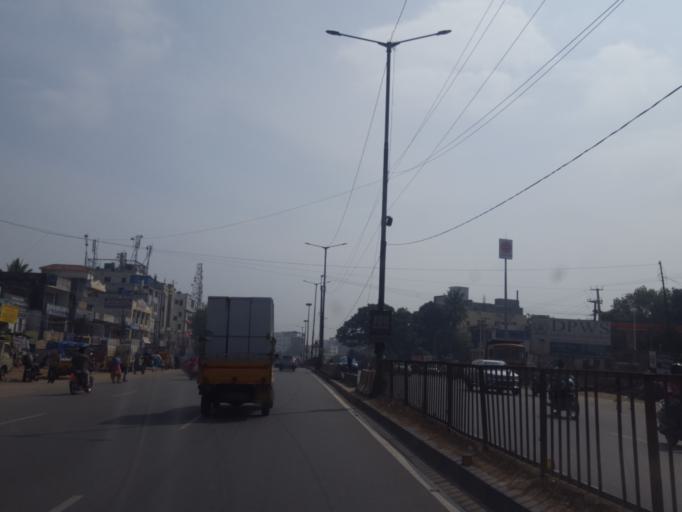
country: IN
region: Telangana
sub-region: Medak
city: Serilingampalle
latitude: 17.5050
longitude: 78.3076
